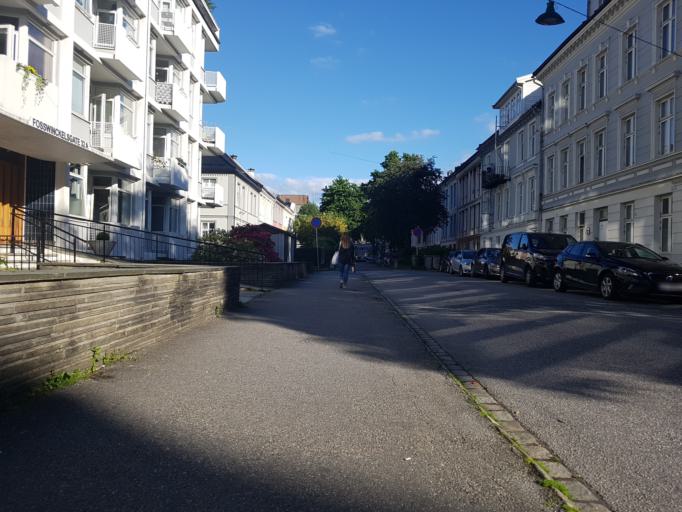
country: NO
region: Hordaland
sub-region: Bergen
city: Bergen
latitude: 60.3872
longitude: 5.3275
